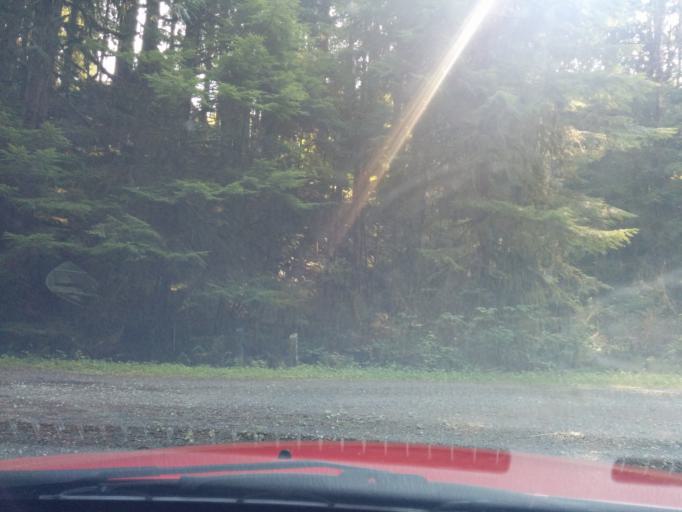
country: US
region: Washington
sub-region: Snohomish County
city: Darrington
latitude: 48.5145
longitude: -121.3702
